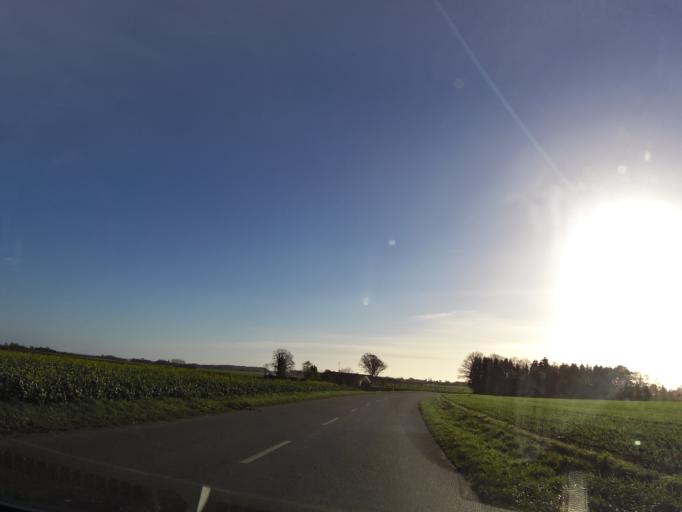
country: DK
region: Central Jutland
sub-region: Odder Kommune
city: Odder
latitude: 55.9513
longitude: 10.2368
